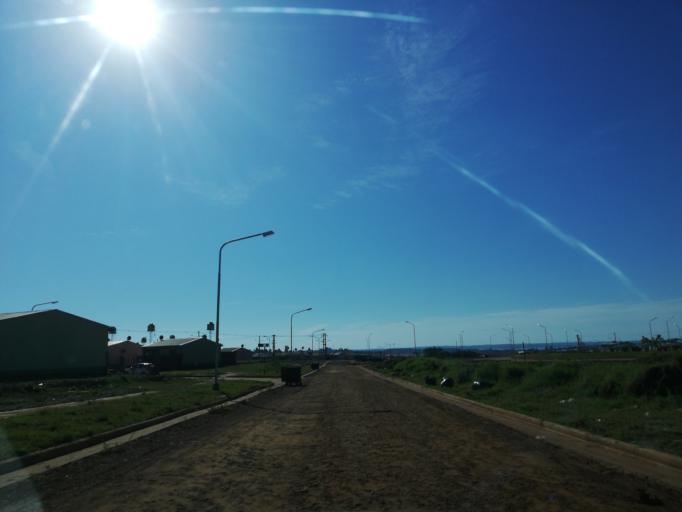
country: AR
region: Misiones
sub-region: Departamento de Capital
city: Posadas
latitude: -27.4161
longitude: -55.9885
